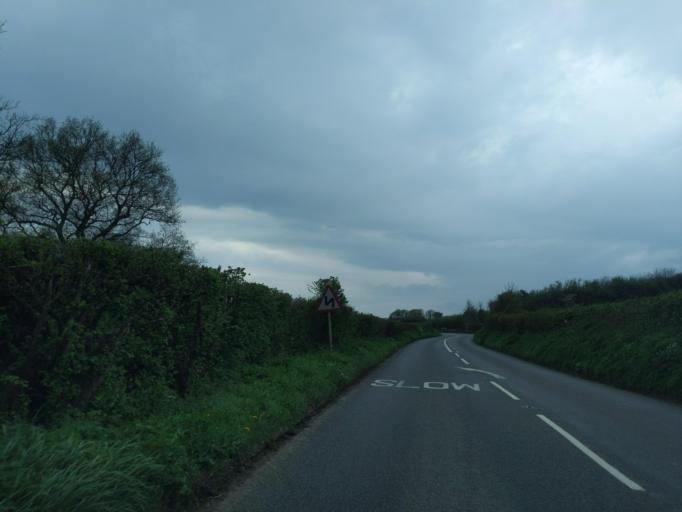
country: GB
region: England
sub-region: Devon
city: Crediton
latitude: 50.7948
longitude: -3.6804
